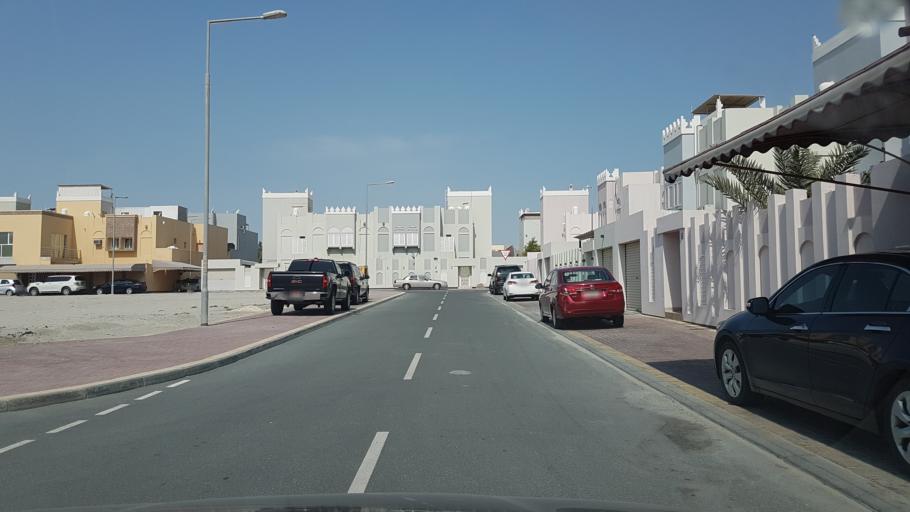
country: BH
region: Northern
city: Madinat `Isa
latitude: 26.1674
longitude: 50.5379
